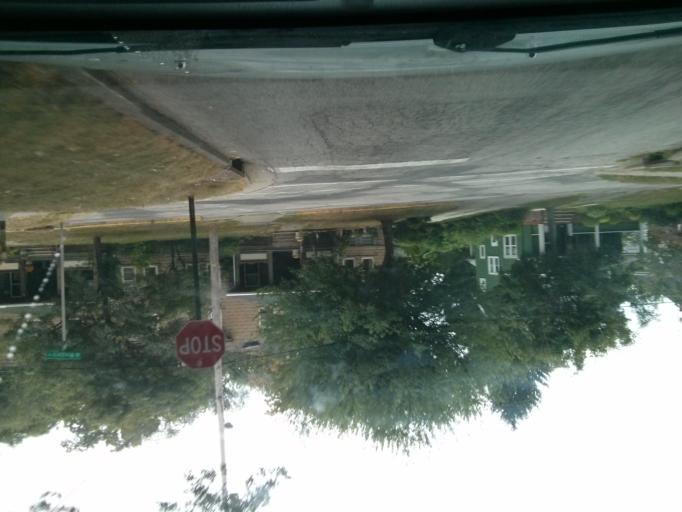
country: US
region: Ohio
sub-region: Portage County
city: Kent
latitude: 41.1579
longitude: -81.3648
